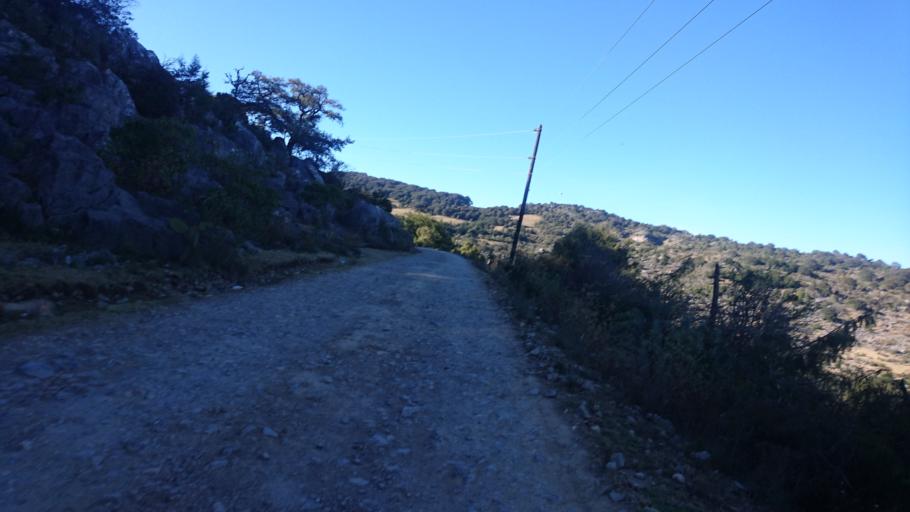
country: MX
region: San Luis Potosi
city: Zaragoza
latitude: 22.0306
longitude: -100.6046
